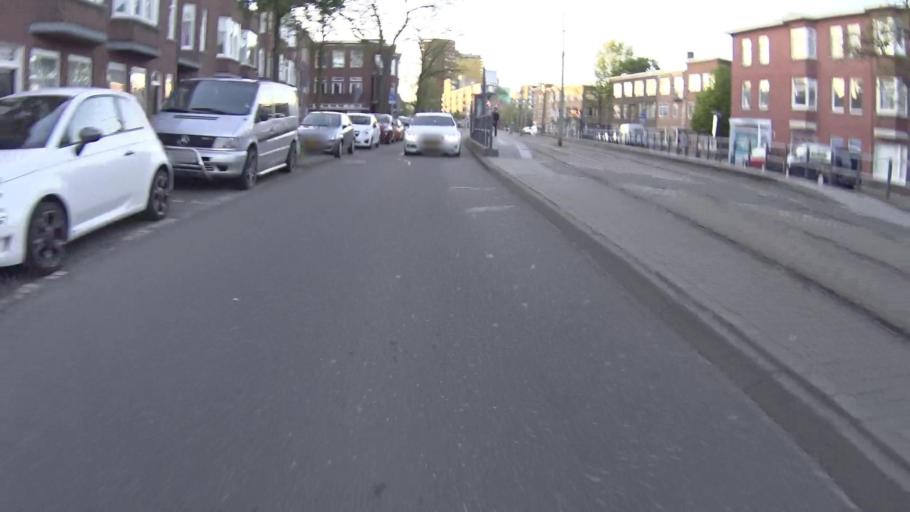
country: NL
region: South Holland
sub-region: Gemeente Rijswijk
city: Rijswijk
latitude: 52.0624
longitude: 4.3255
